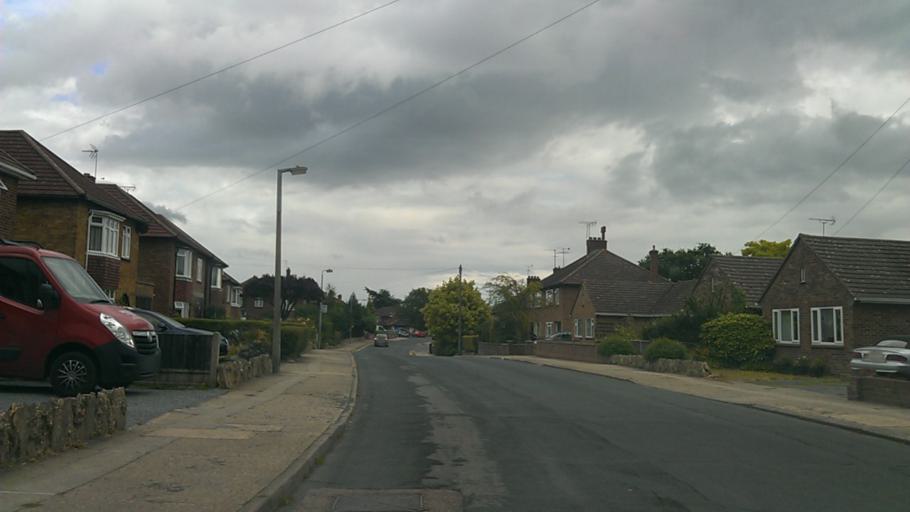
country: GB
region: England
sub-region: Essex
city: West Bergholt
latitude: 51.8799
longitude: 0.8594
